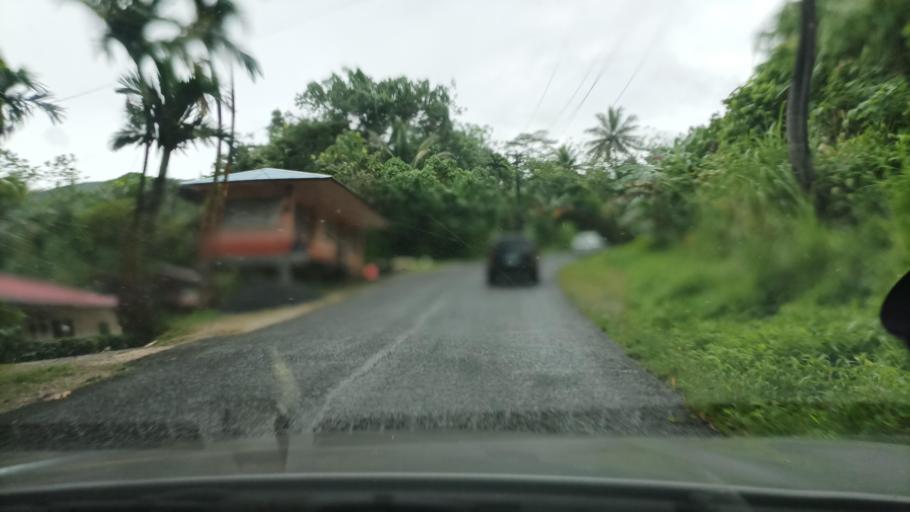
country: FM
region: Pohnpei
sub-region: Sokehs Municipality
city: Palikir - National Government Center
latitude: 6.8834
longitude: 158.1604
